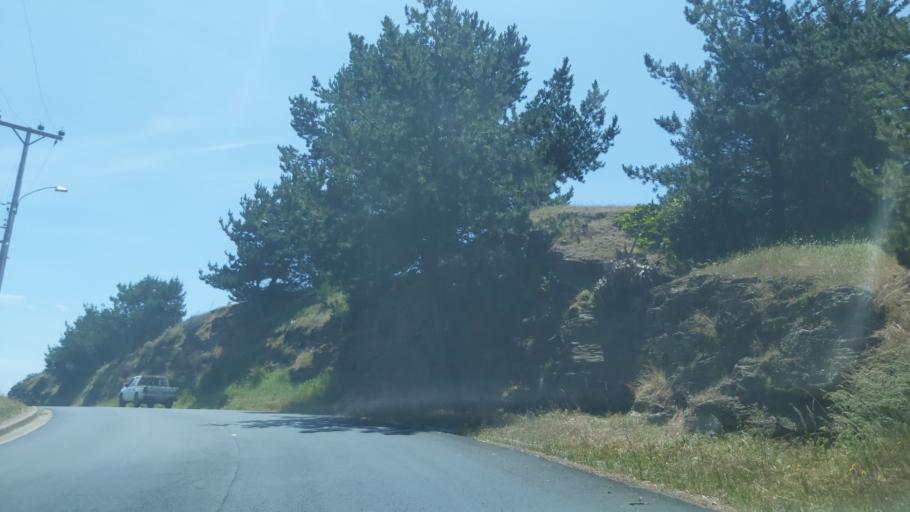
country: CL
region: Maule
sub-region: Provincia de Cauquenes
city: Cauquenes
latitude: -35.8340
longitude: -72.6208
